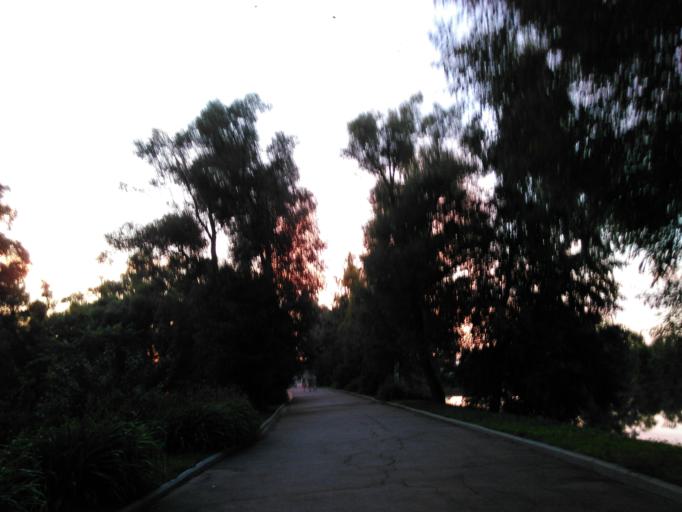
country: RU
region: Penza
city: Lermontovo
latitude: 52.9937
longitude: 43.6741
